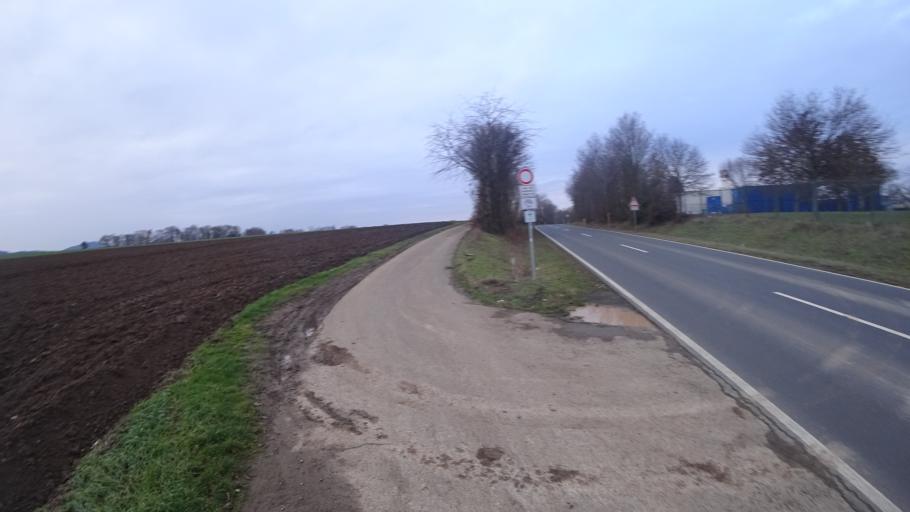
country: DE
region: Rheinland-Pfalz
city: Bassenheim
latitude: 50.3564
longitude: 7.4767
